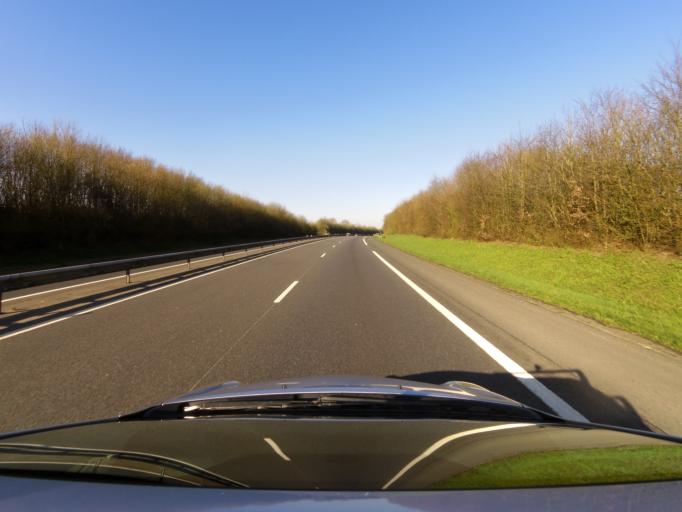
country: FR
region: Lower Normandy
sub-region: Departement du Calvados
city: Saint-Martin-des-Besaces
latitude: 49.0148
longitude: -0.8536
